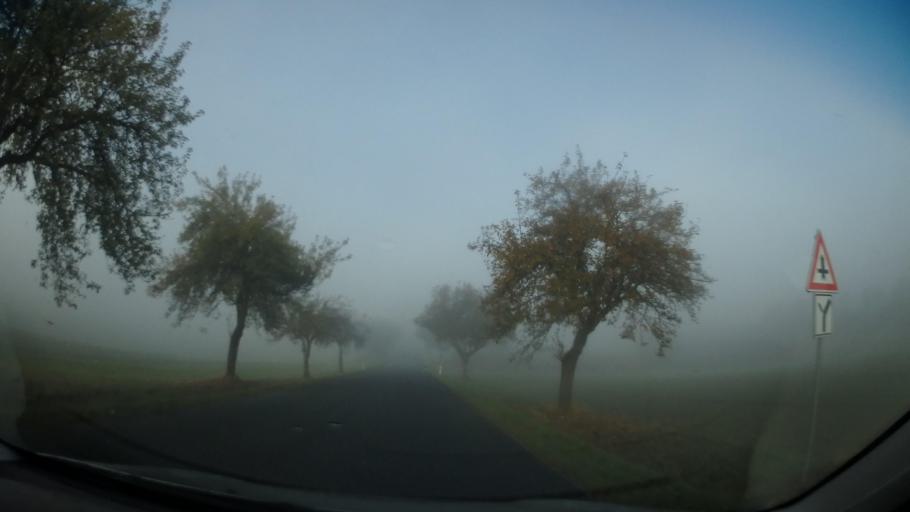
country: CZ
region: Vysocina
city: Krizanov
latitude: 49.4267
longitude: 16.2056
